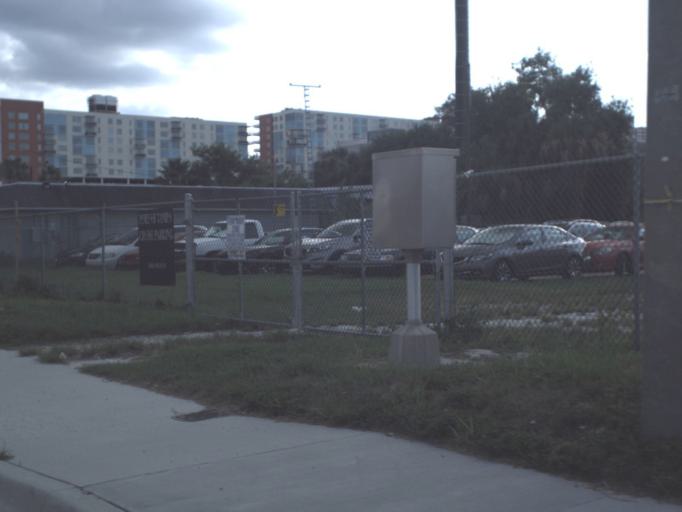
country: US
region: Florida
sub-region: Hillsborough County
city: Tampa
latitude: 27.9539
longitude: -82.4456
